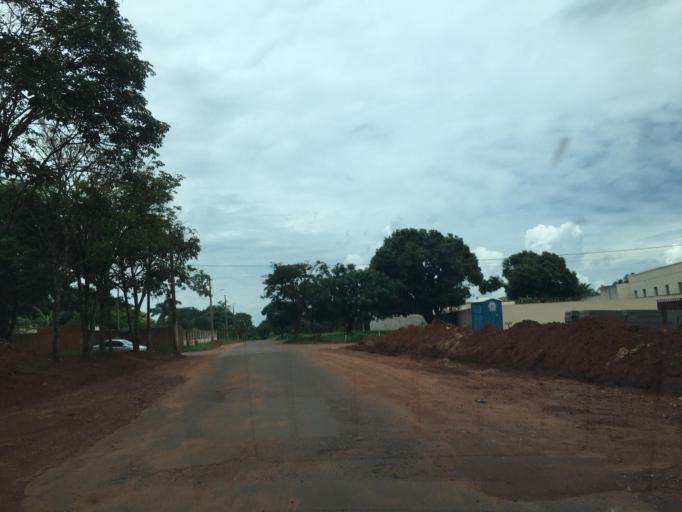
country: BR
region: Minas Gerais
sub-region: Uberlandia
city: Uberlandia
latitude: -18.8648
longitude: -48.2185
